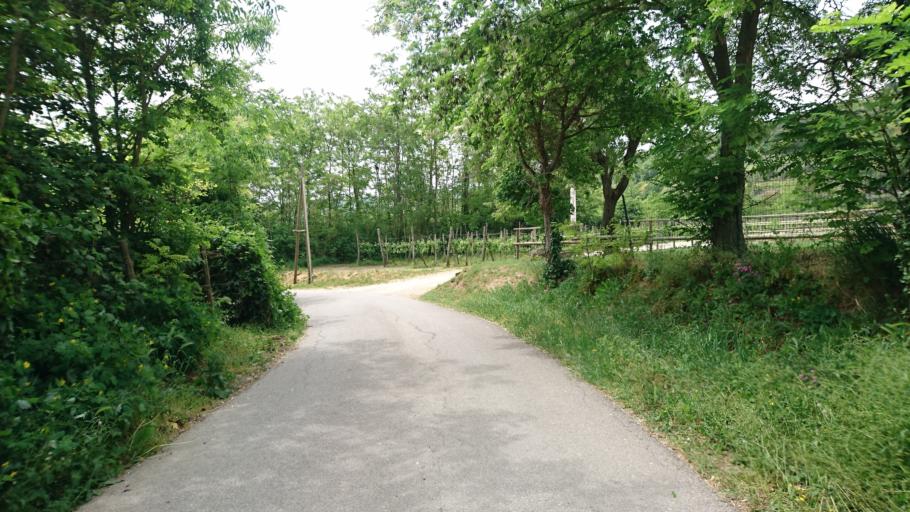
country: IT
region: Veneto
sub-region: Provincia di Padova
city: Arqua Petrarca
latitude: 45.2697
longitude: 11.7136
